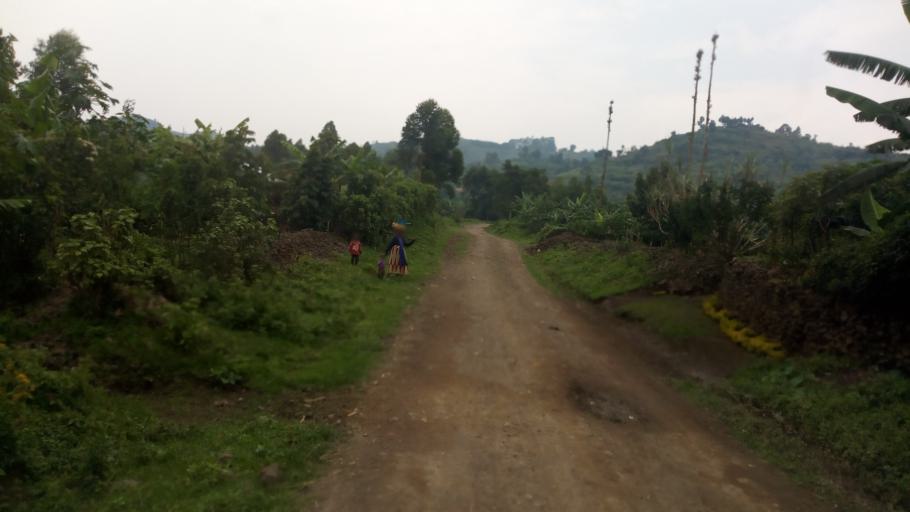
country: UG
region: Western Region
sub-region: Kisoro District
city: Kisoro
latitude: -1.2622
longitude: 29.6276
